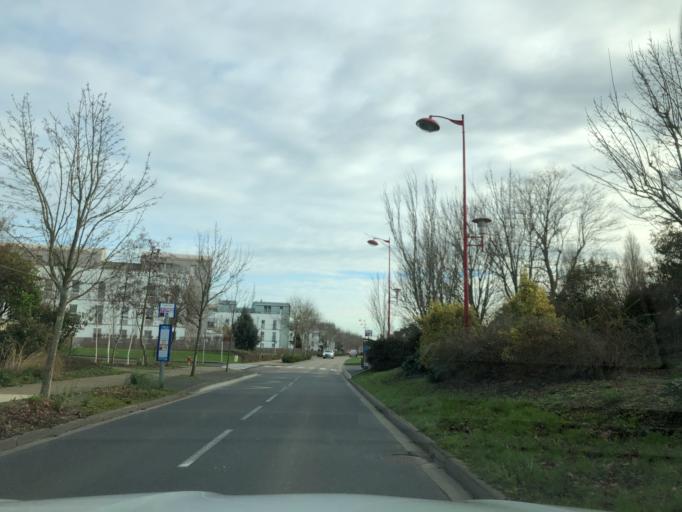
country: FR
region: Lower Normandy
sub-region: Departement du Calvados
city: Blainville-sur-Orne
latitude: 49.2305
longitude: -0.3037
